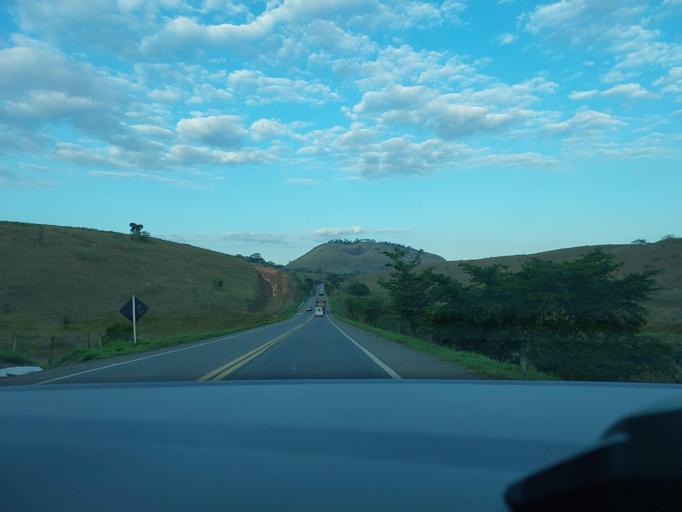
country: BR
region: Rio de Janeiro
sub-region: Natividade
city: Natividade
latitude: -21.1544
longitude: -42.1372
